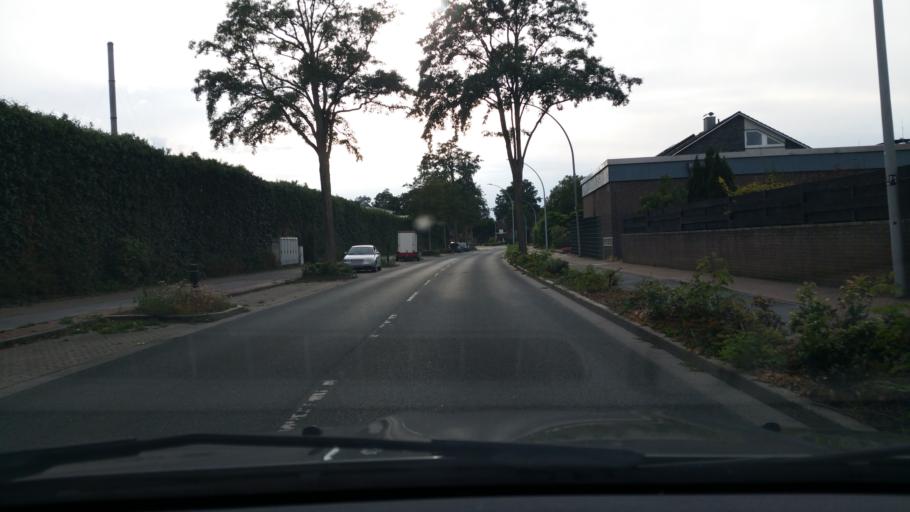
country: DE
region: North Rhine-Westphalia
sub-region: Regierungsbezirk Dusseldorf
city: Bocholt
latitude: 51.8475
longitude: 6.6233
